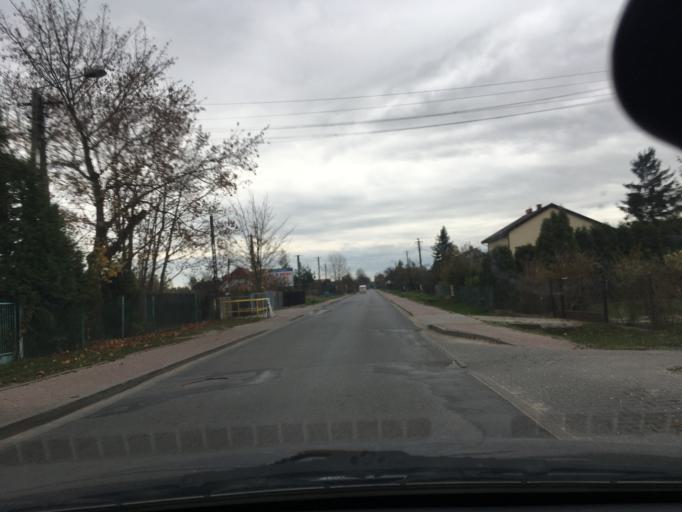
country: PL
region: Lodz Voivodeship
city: Zabia Wola
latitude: 52.0307
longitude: 20.6911
